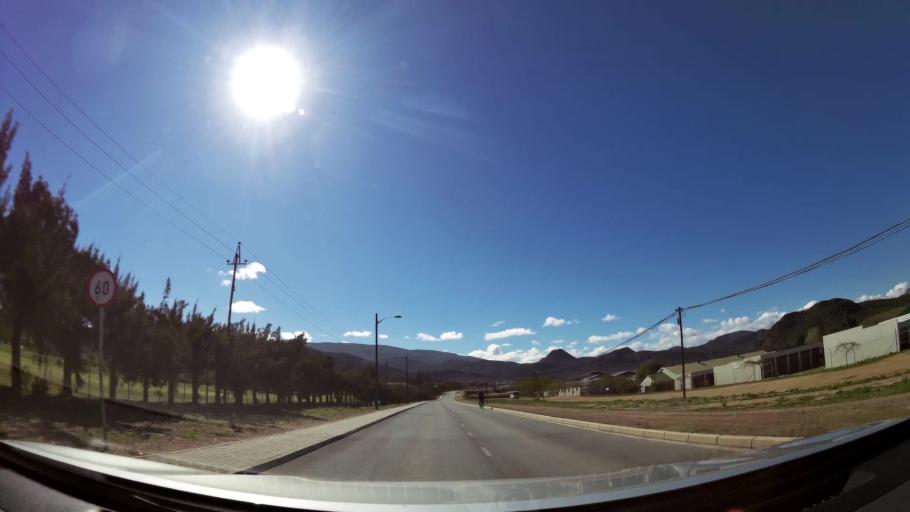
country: ZA
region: Western Cape
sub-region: Cape Winelands District Municipality
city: Ashton
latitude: -33.7751
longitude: 20.1335
